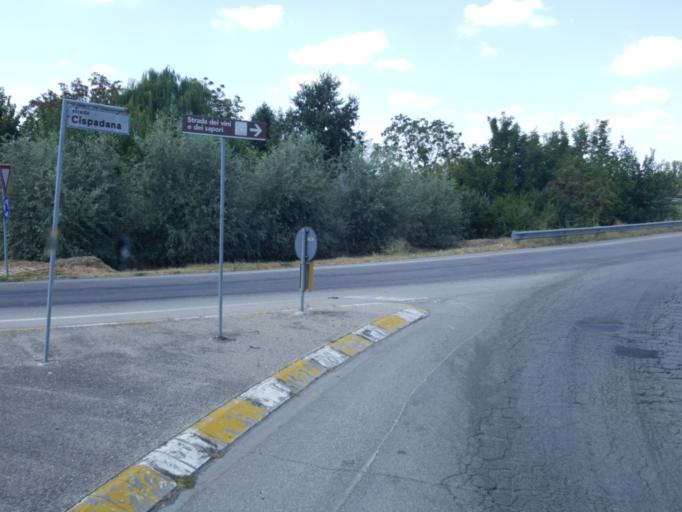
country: IT
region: Lombardy
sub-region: Provincia di Mantova
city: Bondeno
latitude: 44.9158
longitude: 10.8461
